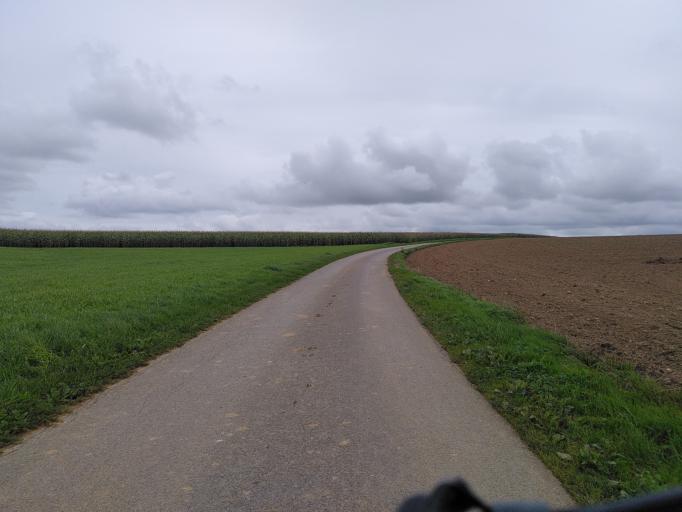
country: FR
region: Nord-Pas-de-Calais
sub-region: Departement du Pas-de-Calais
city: Desvres
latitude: 50.6560
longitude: 1.9239
